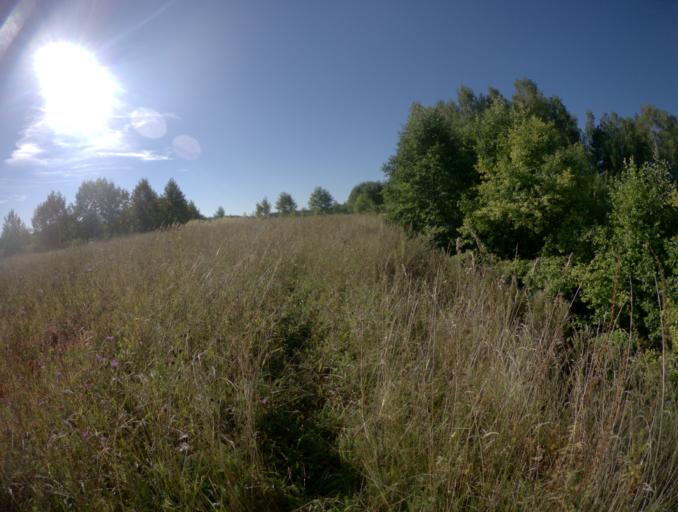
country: RU
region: Vladimir
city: Nikologory
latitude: 56.1767
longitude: 41.9429
